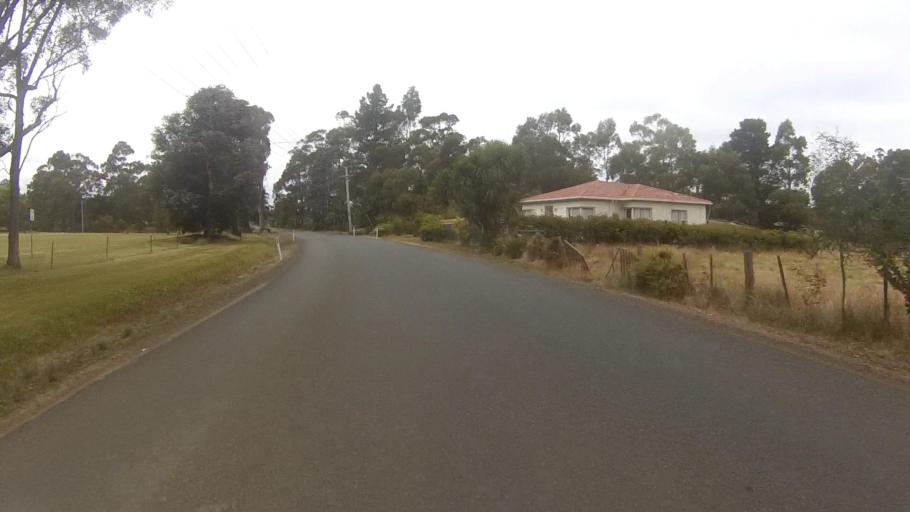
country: AU
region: Tasmania
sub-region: Kingborough
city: Margate
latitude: -42.9640
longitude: 147.2343
